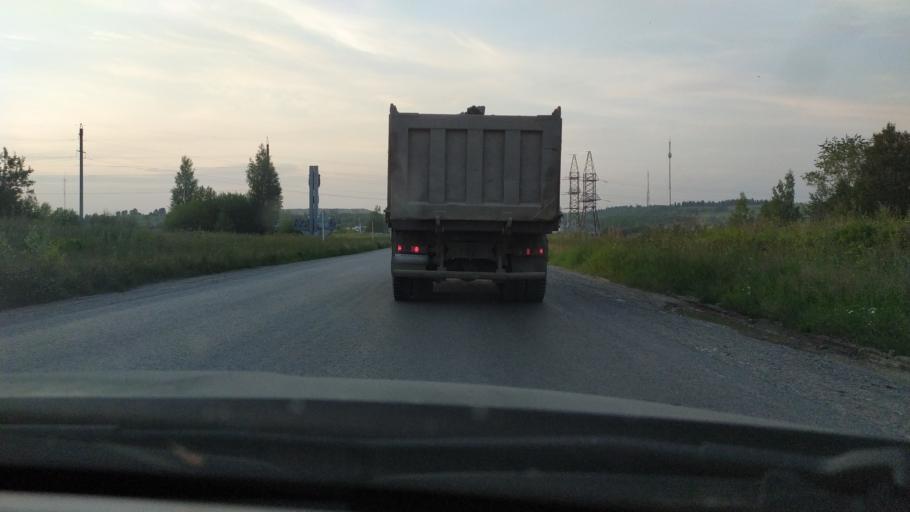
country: RU
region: Perm
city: Chusovoy
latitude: 58.3083
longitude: 57.8293
